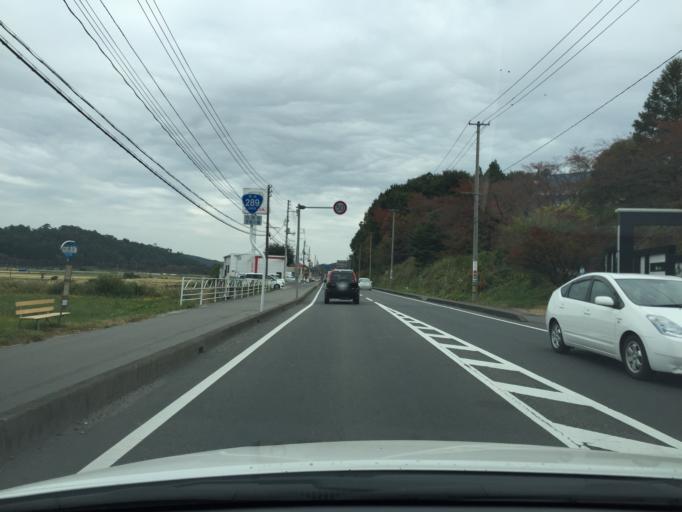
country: JP
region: Tochigi
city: Kuroiso
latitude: 37.1139
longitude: 140.2021
